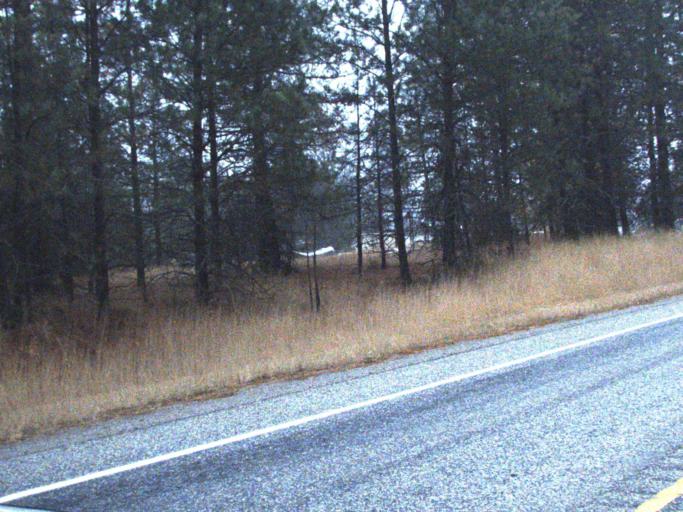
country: US
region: Washington
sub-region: Stevens County
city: Kettle Falls
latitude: 48.7093
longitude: -118.1276
